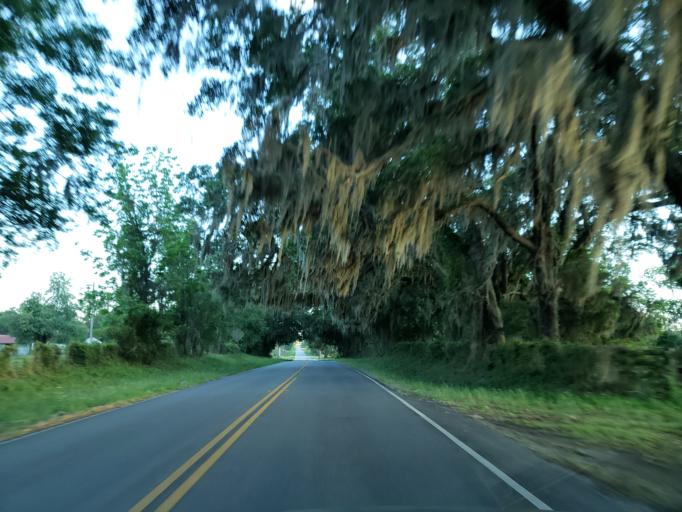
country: US
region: Georgia
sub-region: Lowndes County
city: Valdosta
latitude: 30.7156
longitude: -83.2428
